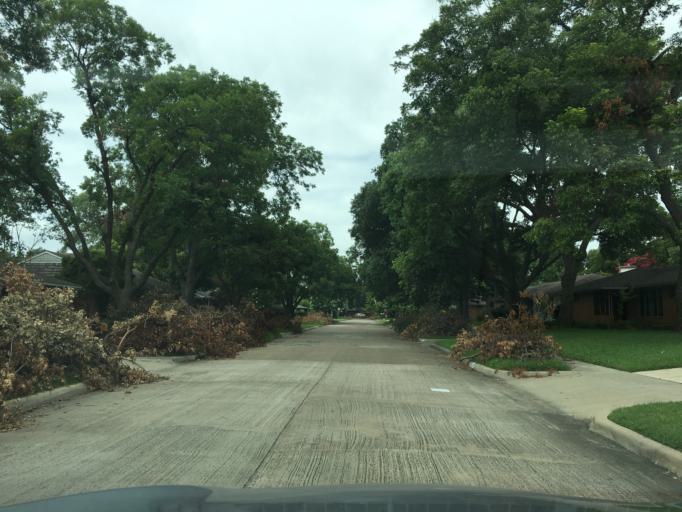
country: US
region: Texas
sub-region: Dallas County
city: Highland Park
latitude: 32.8609
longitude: -96.7424
